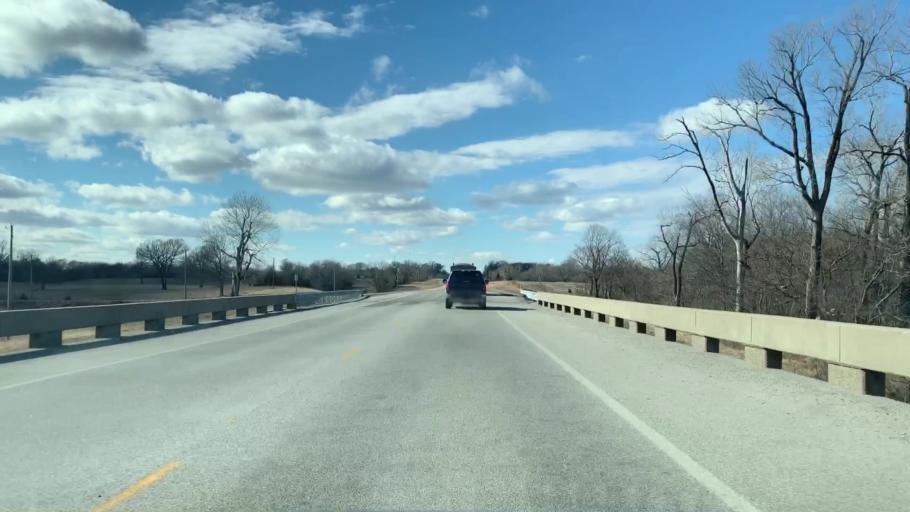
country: US
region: Kansas
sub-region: Cherokee County
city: Columbus
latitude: 37.3399
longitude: -94.8853
